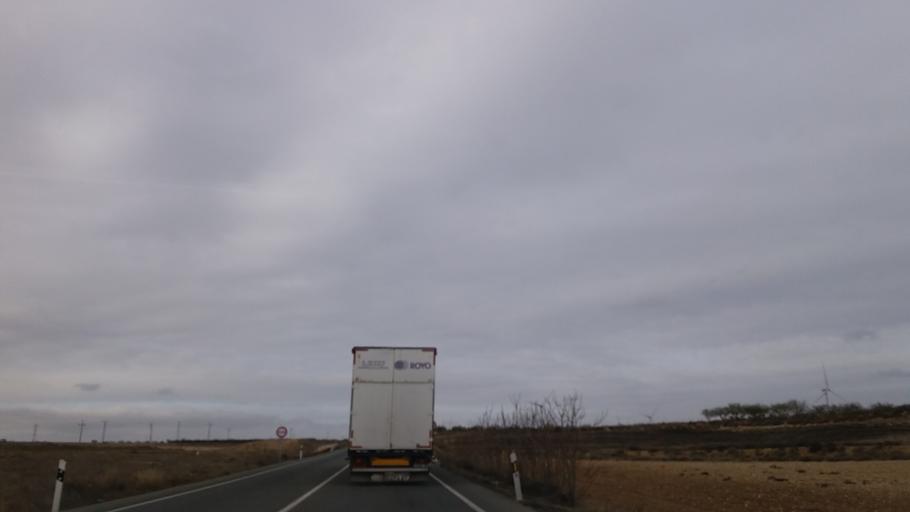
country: ES
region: Aragon
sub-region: Provincia de Zaragoza
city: Mallen
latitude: 41.8671
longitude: -1.3869
